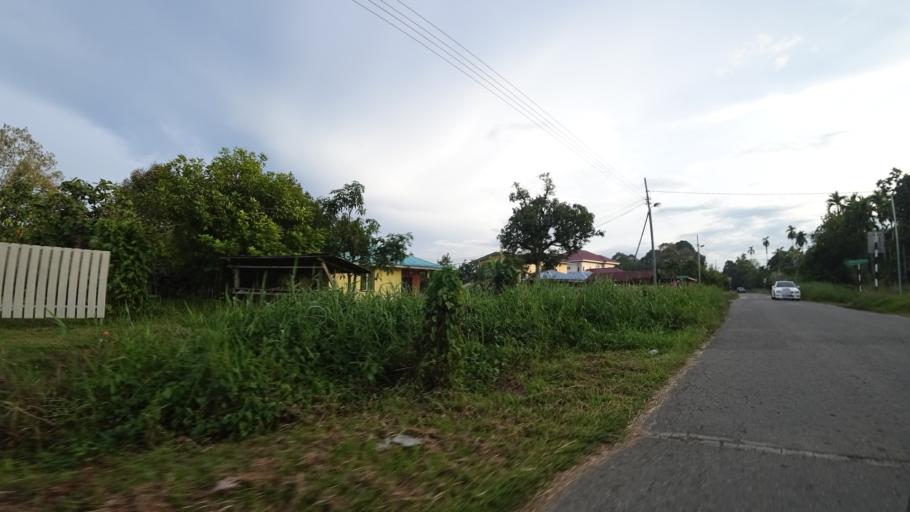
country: BN
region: Brunei and Muara
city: Bandar Seri Begawan
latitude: 4.8135
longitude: 114.8279
